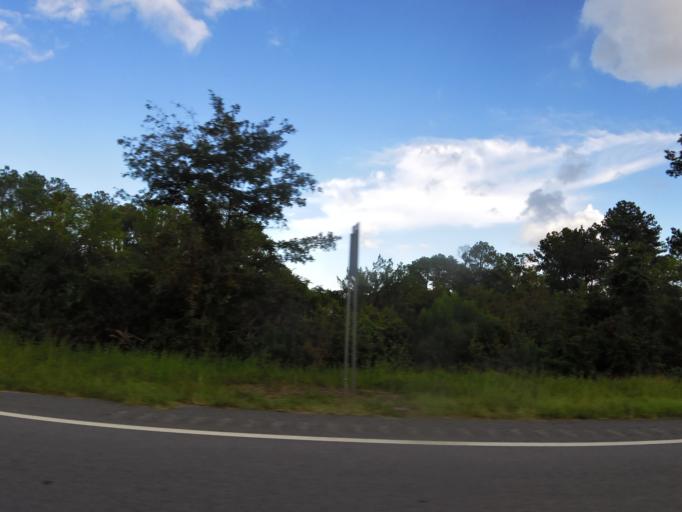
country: US
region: Georgia
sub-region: Glynn County
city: Country Club Estates
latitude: 31.2019
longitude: -81.4676
